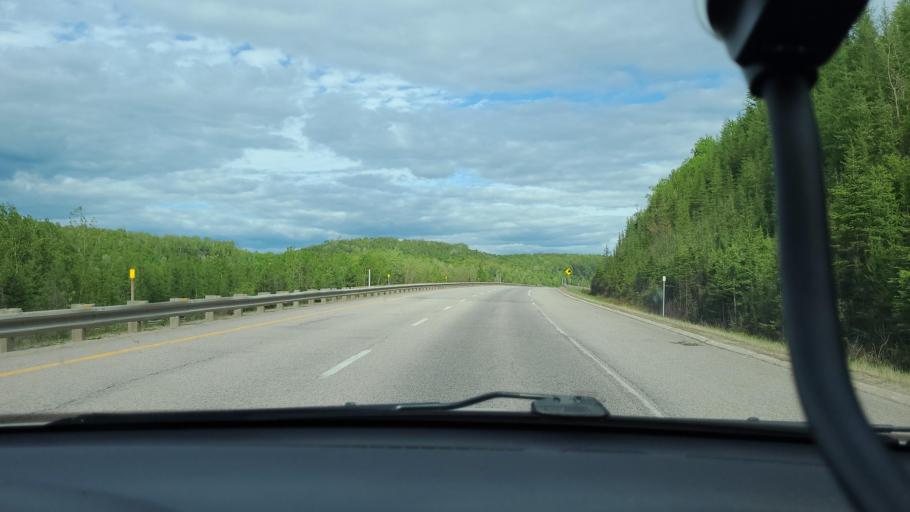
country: CA
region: Quebec
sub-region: Laurentides
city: Mont-Tremblant
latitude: 46.1393
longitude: -74.6409
